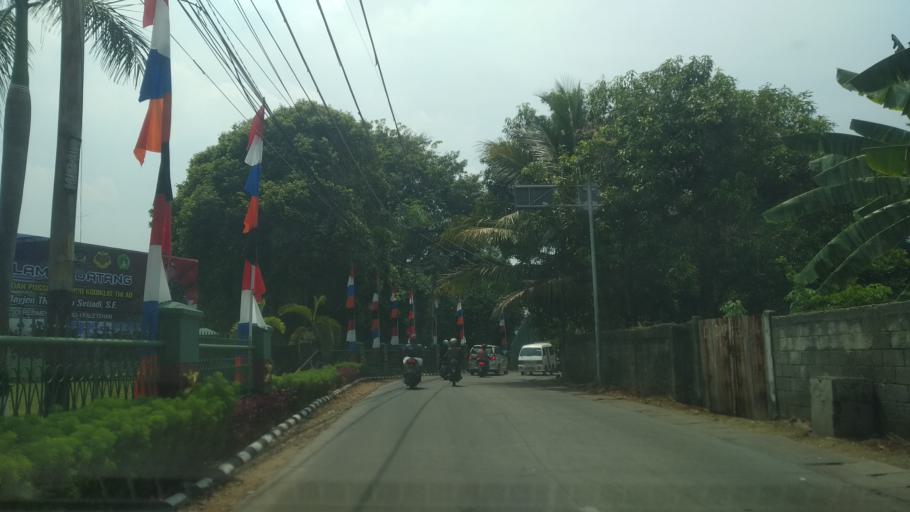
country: ID
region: Banten
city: South Tangerang
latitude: -6.2622
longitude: 106.7535
